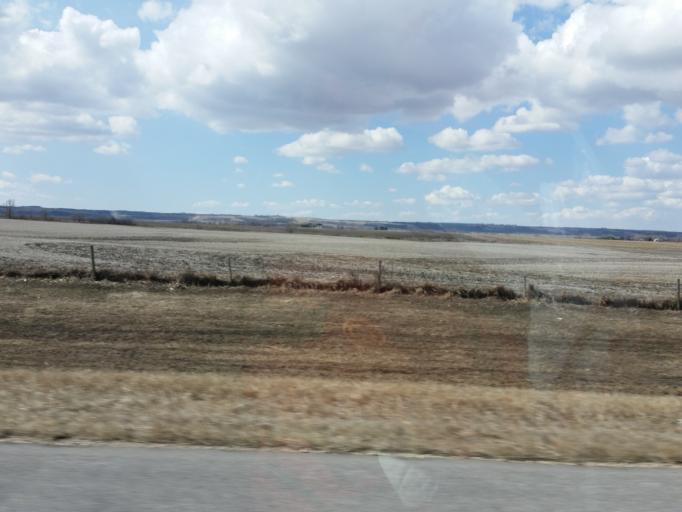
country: US
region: South Dakota
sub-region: Roberts County
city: Sisseton
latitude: 45.5105
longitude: -96.9896
